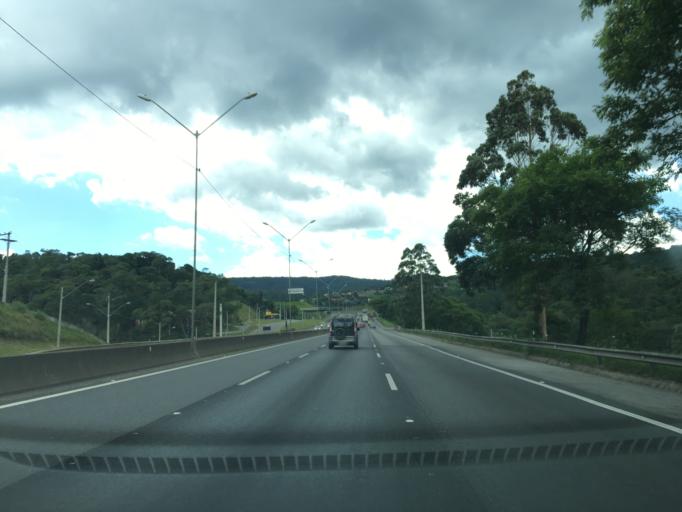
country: BR
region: Sao Paulo
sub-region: Mairipora
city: Mairipora
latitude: -23.3378
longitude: -46.5751
